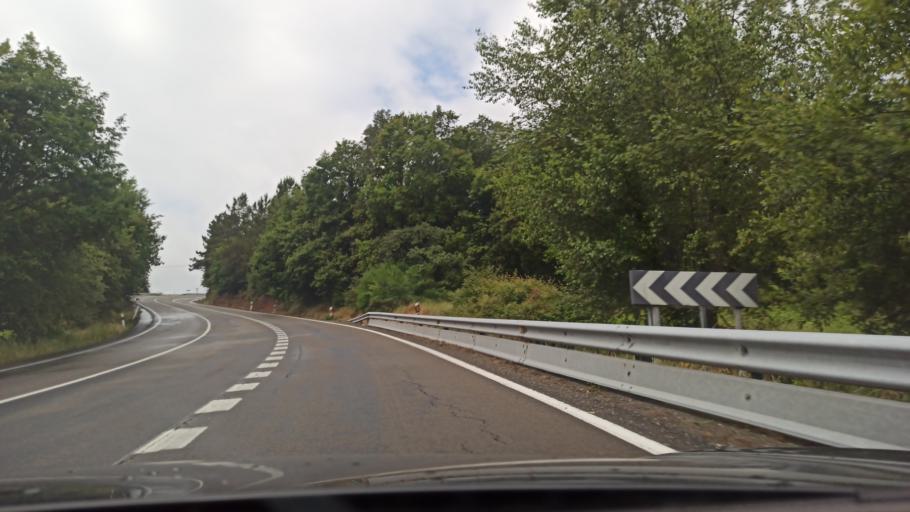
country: ES
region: Galicia
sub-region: Provincia de Lugo
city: Monterroso
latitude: 42.7778
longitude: -7.9367
